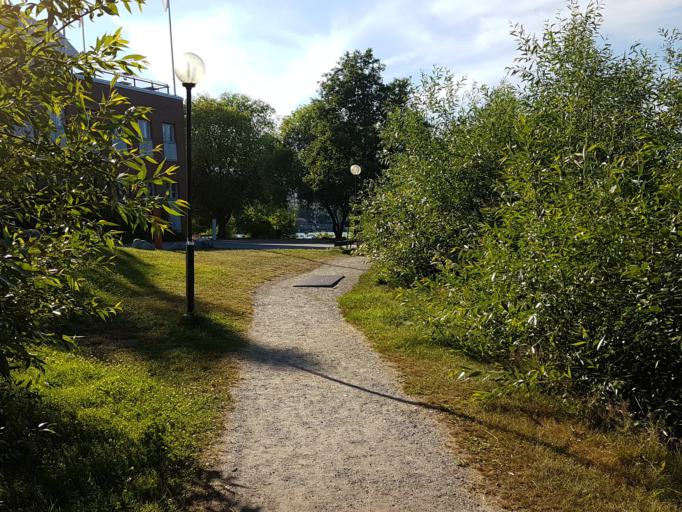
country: SE
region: Stockholm
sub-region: Solna Kommun
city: Solna
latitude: 59.3265
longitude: 17.9917
